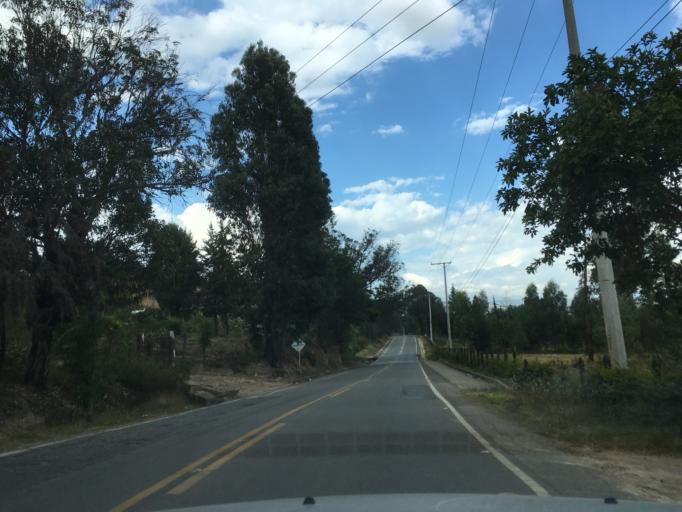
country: CO
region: Boyaca
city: Sutamarchan
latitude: 5.6020
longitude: -73.6369
